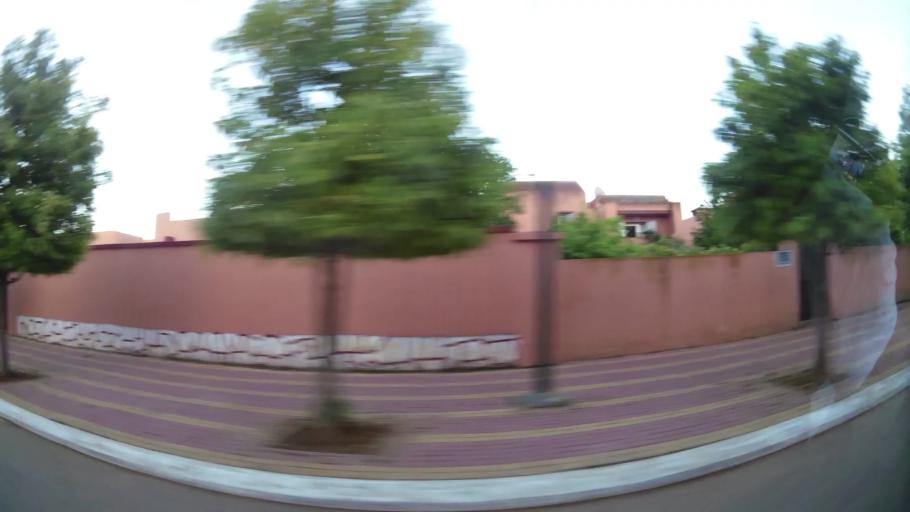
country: MA
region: Marrakech-Tensift-Al Haouz
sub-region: Kelaa-Des-Sraghna
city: Sidi Bou Othmane
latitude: 32.2106
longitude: -7.9321
